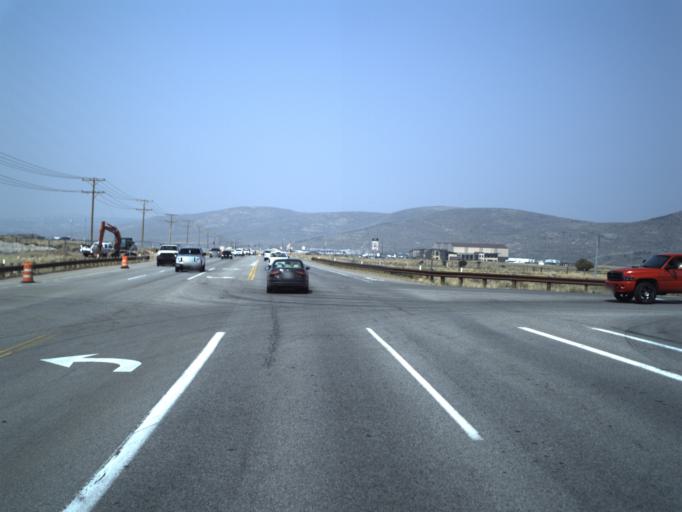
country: US
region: Utah
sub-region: Summit County
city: Park City
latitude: 40.6742
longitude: -111.4693
